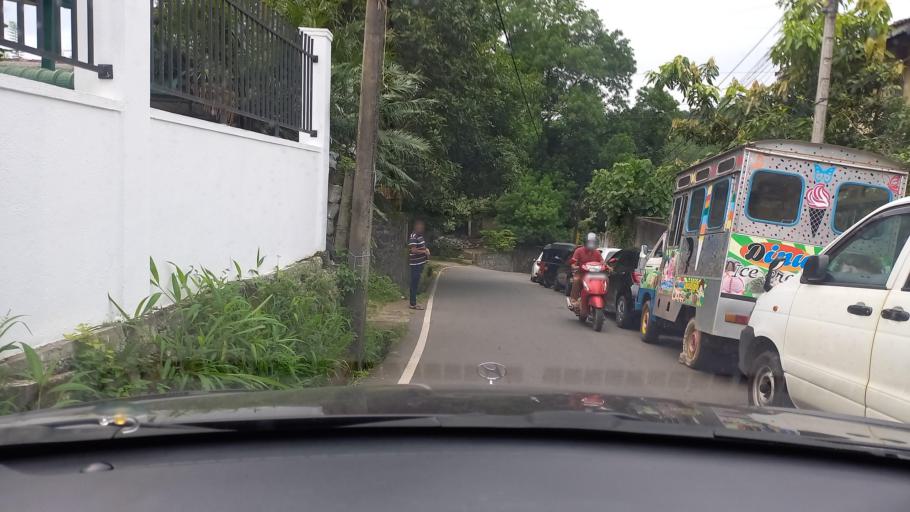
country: LK
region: Central
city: Kadugannawa
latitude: 7.2567
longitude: 80.3510
